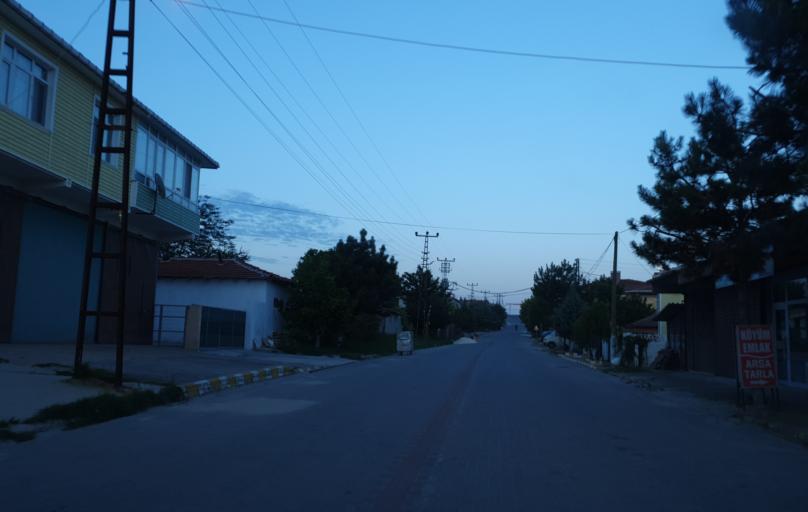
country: TR
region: Tekirdag
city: Velimese
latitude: 41.3487
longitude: 27.8858
